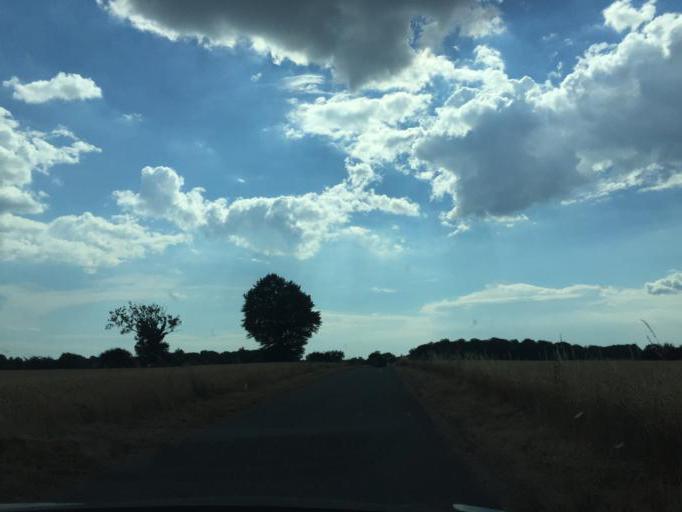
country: DK
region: South Denmark
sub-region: Assens Kommune
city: Glamsbjerg
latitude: 55.2170
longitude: 10.0128
